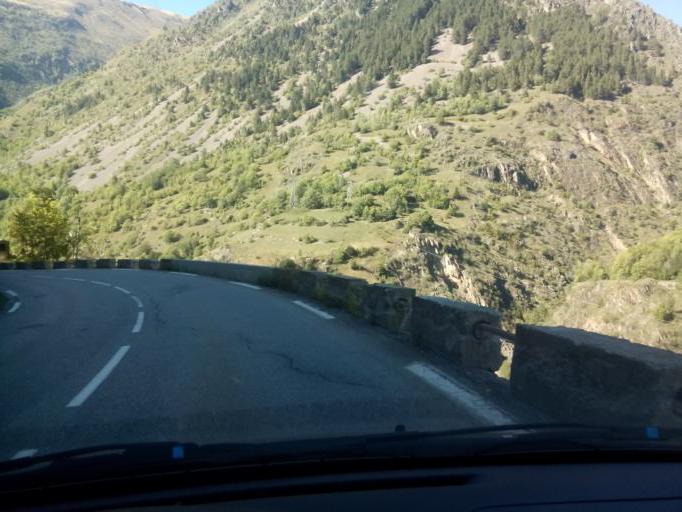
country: FR
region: Rhone-Alpes
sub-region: Departement de l'Isere
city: Mont-de-Lans
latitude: 45.0463
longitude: 6.1350
